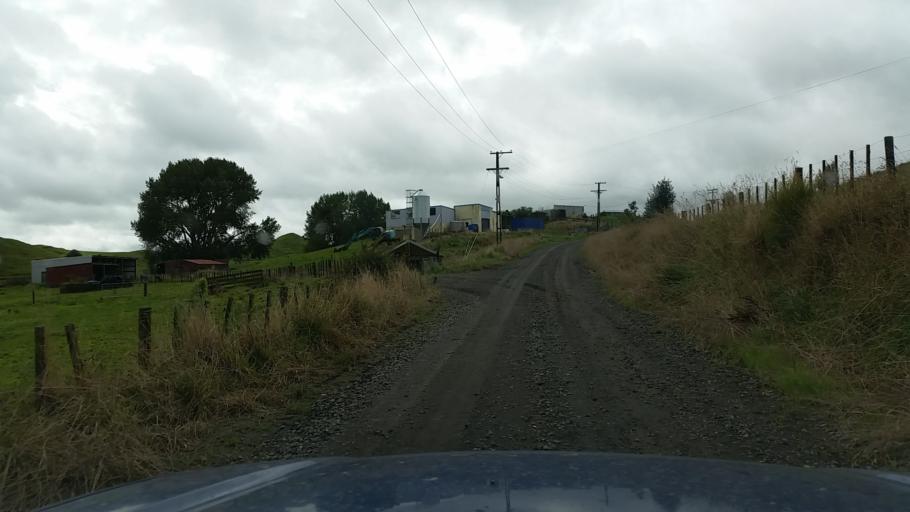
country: NZ
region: Taranaki
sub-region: South Taranaki District
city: Eltham
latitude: -39.3524
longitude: 174.4352
